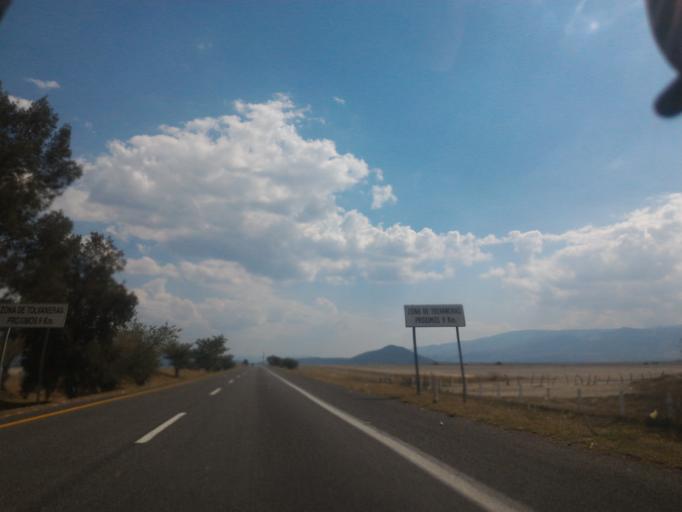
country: MX
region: Jalisco
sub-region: Acatlan de Juarez
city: Villa de los Ninos
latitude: 20.3289
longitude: -103.5682
